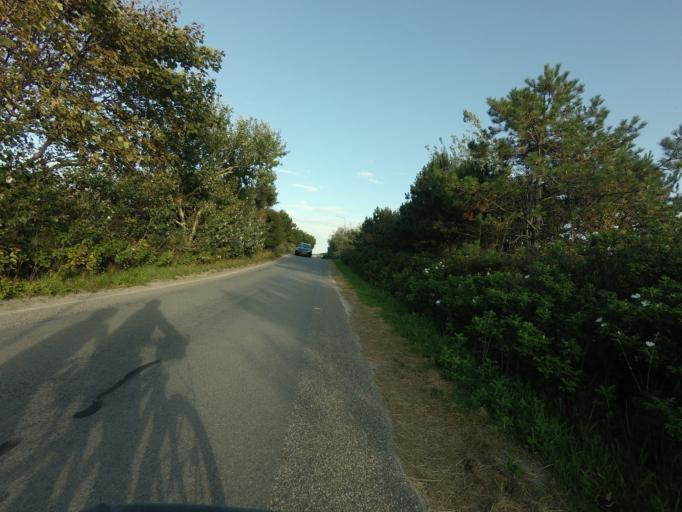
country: NL
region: Friesland
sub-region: Gemeente Ameland
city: Nes
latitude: 53.4568
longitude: 5.8016
